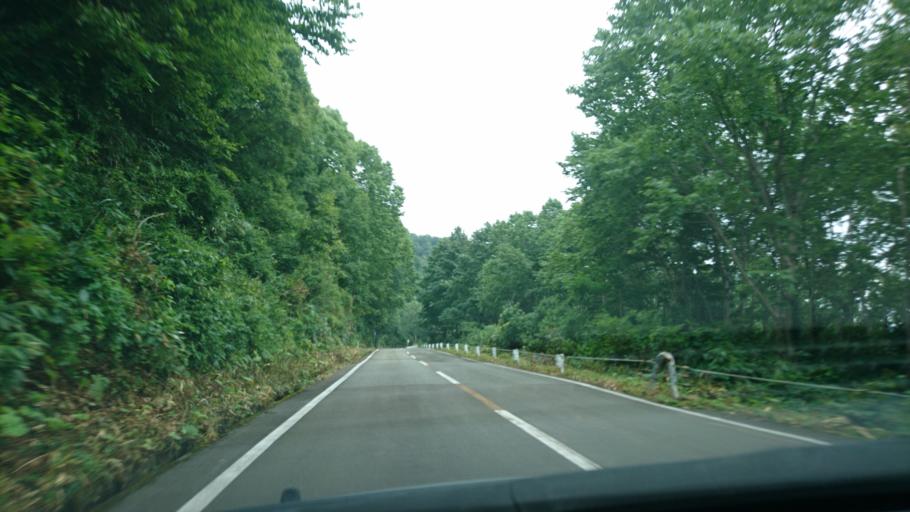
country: JP
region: Akita
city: Yuzawa
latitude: 38.9752
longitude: 140.7220
